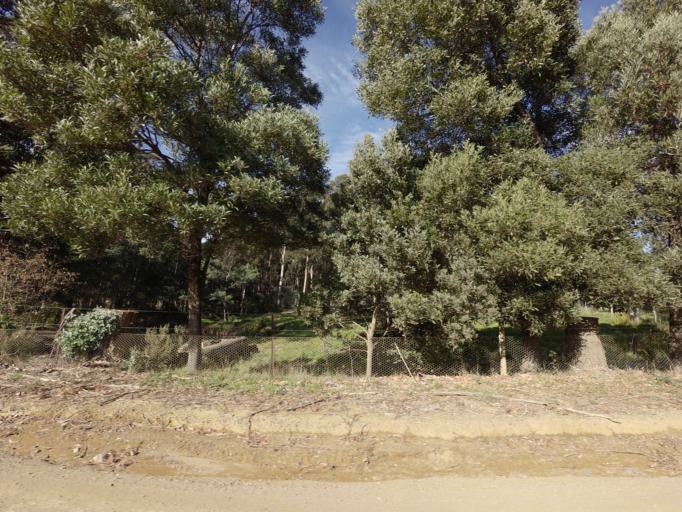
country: AU
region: Tasmania
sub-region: Clarence
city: Sandford
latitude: -43.1429
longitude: 147.7656
